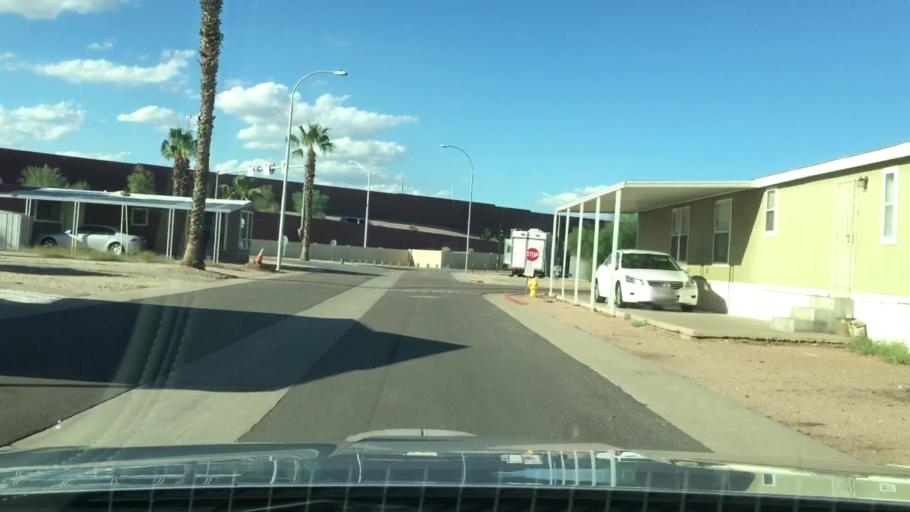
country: US
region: Arizona
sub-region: Maricopa County
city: Mesa
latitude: 33.4500
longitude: -111.8476
